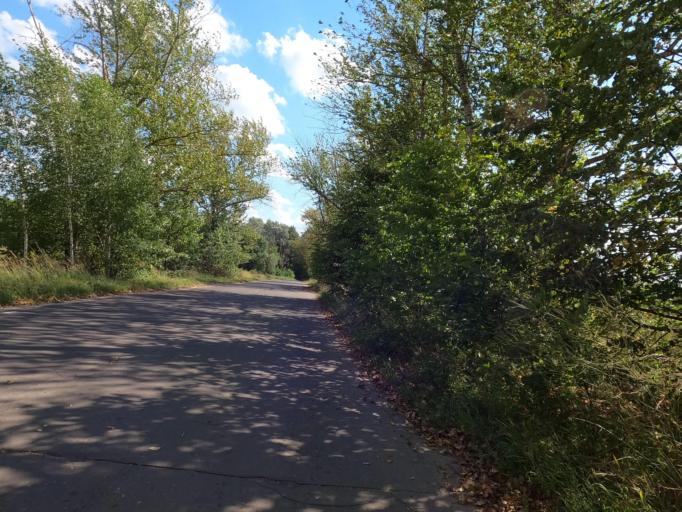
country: RU
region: Moskovskaya
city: Peski
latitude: 55.2241
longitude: 38.7521
